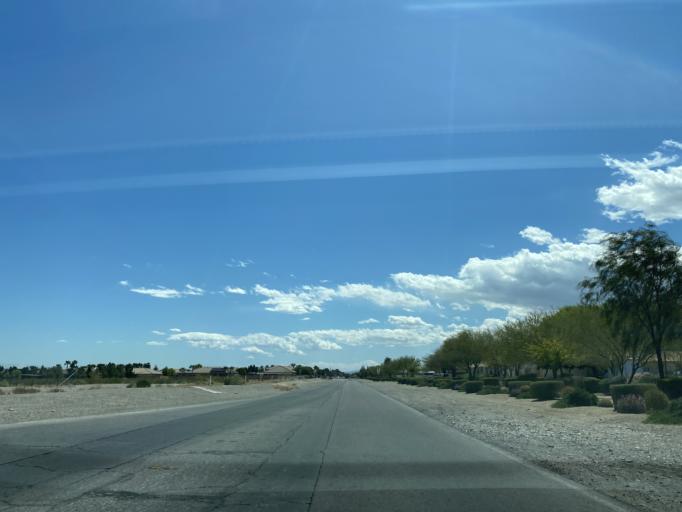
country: US
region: Nevada
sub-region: Clark County
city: North Las Vegas
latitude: 36.3049
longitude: -115.2422
